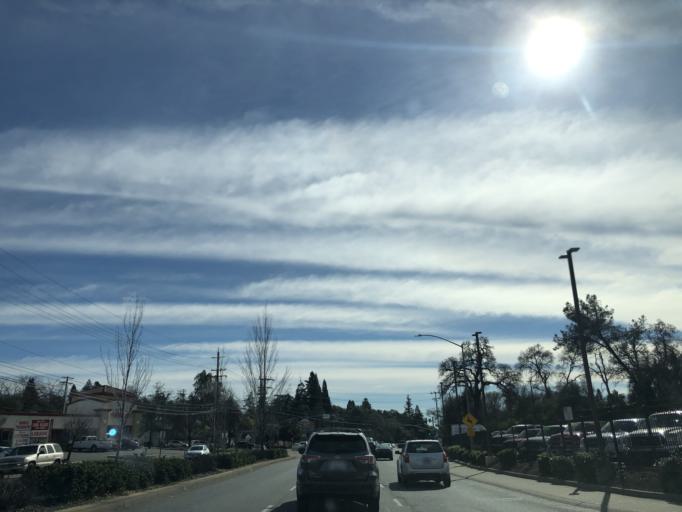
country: US
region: California
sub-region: Sacramento County
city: Fair Oaks
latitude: 38.6417
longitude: -121.2724
